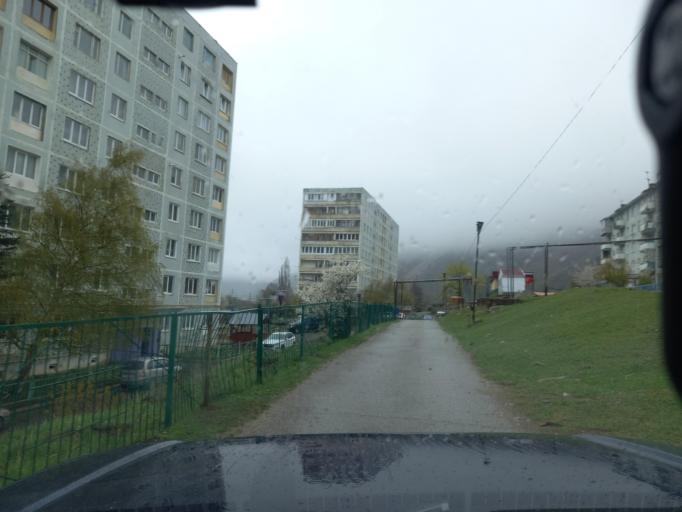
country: RU
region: Kabardino-Balkariya
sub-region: El'brusskiy Rayon
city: El'brus
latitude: 43.2768
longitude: 42.6862
